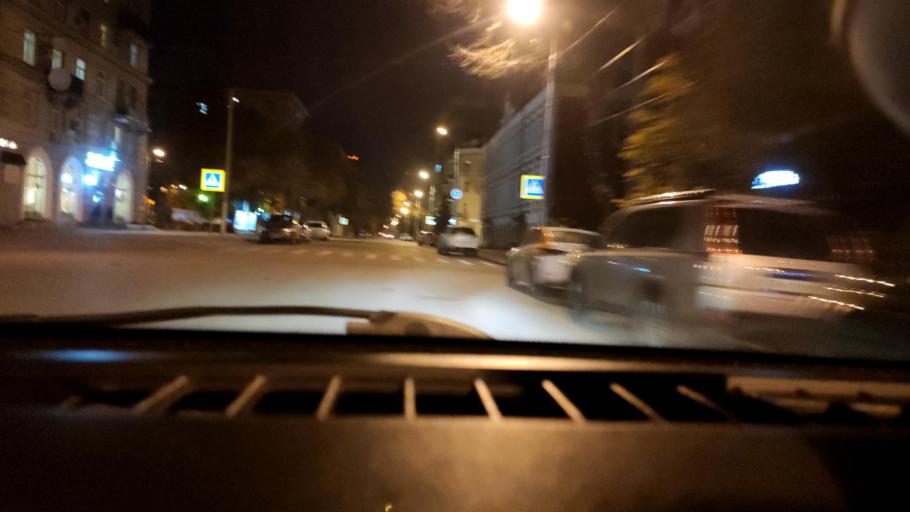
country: RU
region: Samara
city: Samara
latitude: 53.1991
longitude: 50.1132
